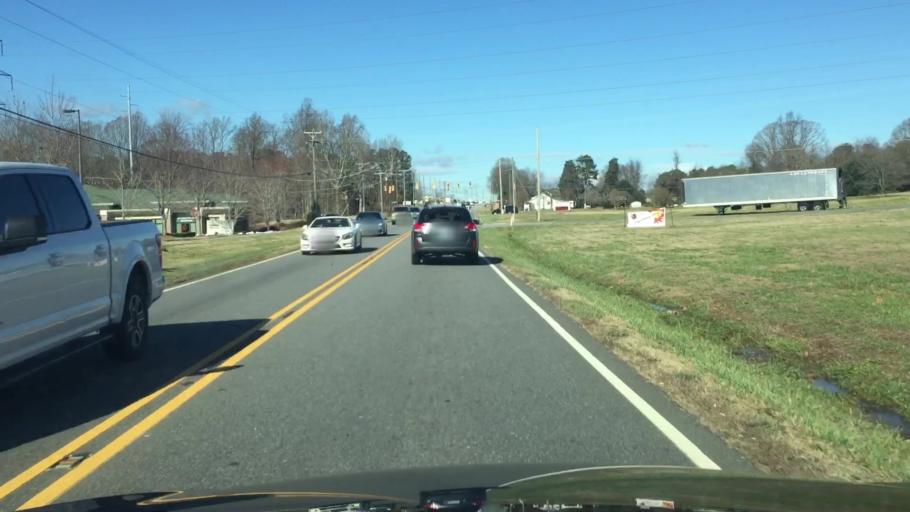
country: US
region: North Carolina
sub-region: Iredell County
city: Mooresville
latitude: 35.5767
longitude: -80.8705
